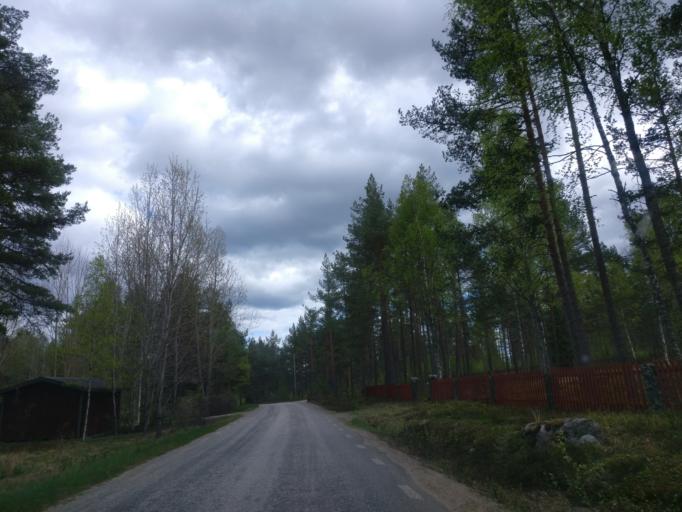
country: SE
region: Gaevleborg
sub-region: Soderhamns Kommun
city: Marielund
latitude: 61.4579
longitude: 17.1025
